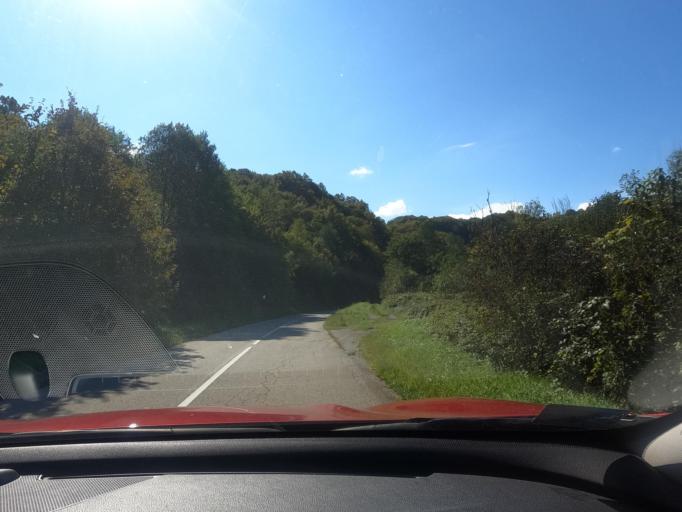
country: BA
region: Federation of Bosnia and Herzegovina
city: Vrnograc
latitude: 45.2670
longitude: 15.9719
